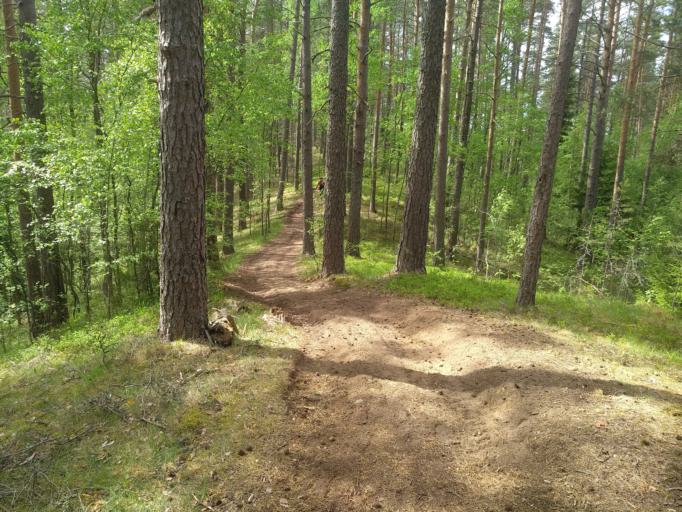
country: RU
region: Leningrad
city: Michurinskoye
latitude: 60.5954
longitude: 29.8843
